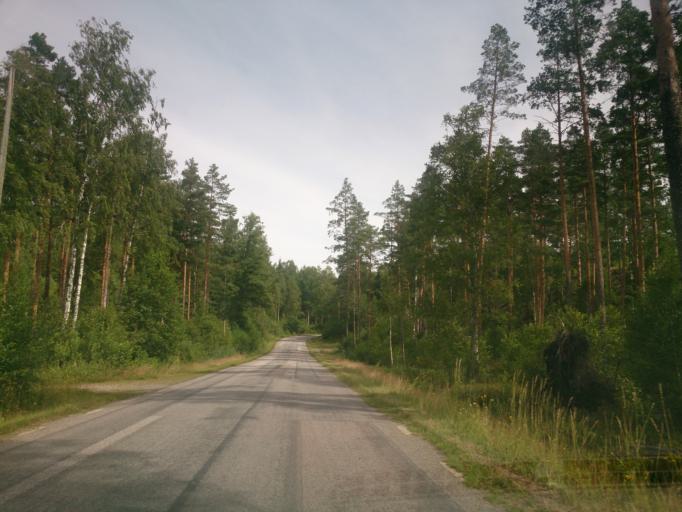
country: SE
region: OEstergoetland
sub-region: Soderkopings Kommun
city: Soederkoeping
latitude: 58.2916
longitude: 16.2452
